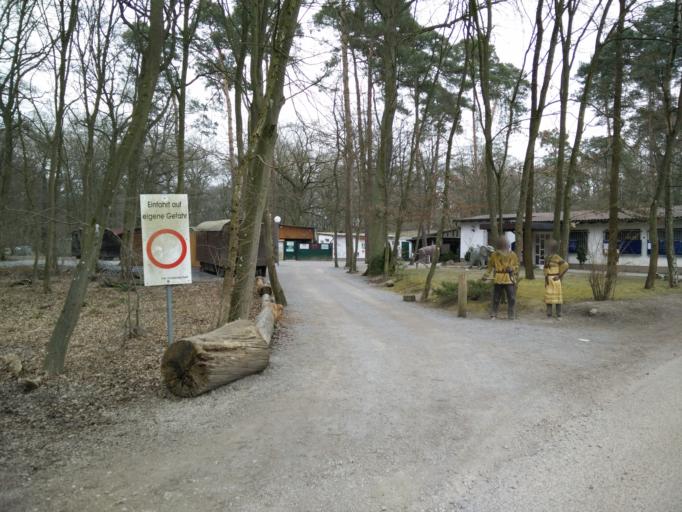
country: DE
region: Rheinland-Pfalz
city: Schifferstadt
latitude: 49.3682
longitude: 8.3838
